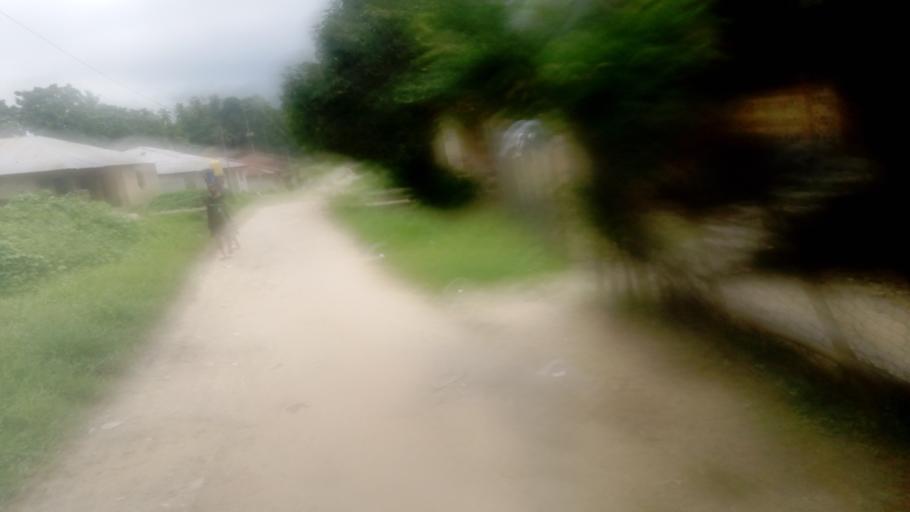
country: SL
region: Northern Province
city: Lunsar
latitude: 8.6797
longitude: -12.5381
